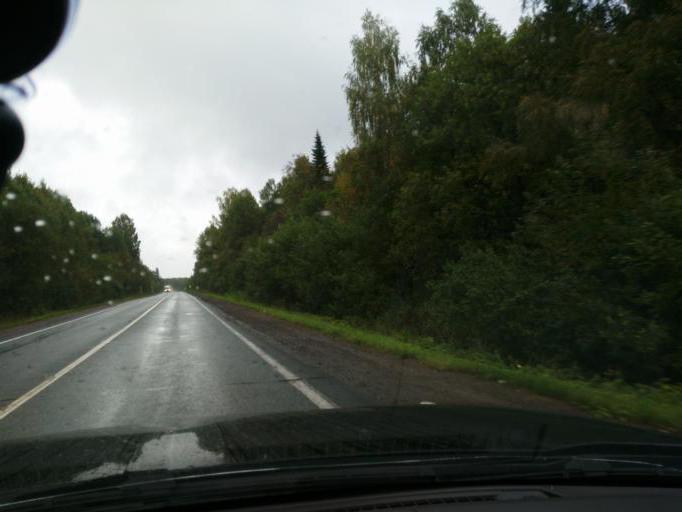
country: RU
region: Perm
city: Yugo-Kamskiy
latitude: 57.7357
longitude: 55.7083
